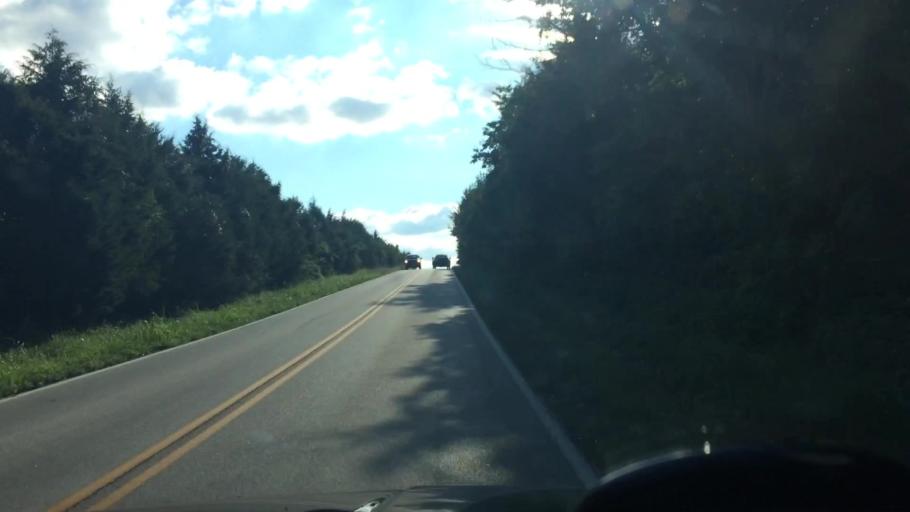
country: US
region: Missouri
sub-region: Greene County
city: Strafford
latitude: 37.2862
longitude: -93.0948
